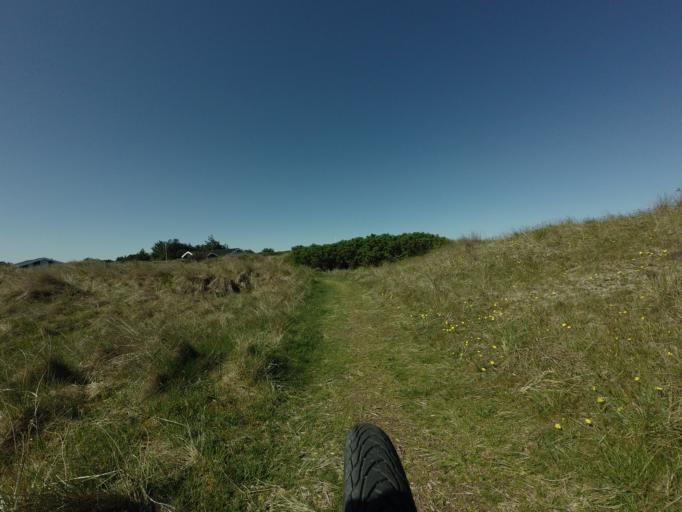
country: DK
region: North Denmark
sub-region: Jammerbugt Kommune
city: Pandrup
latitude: 57.3129
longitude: 9.6593
